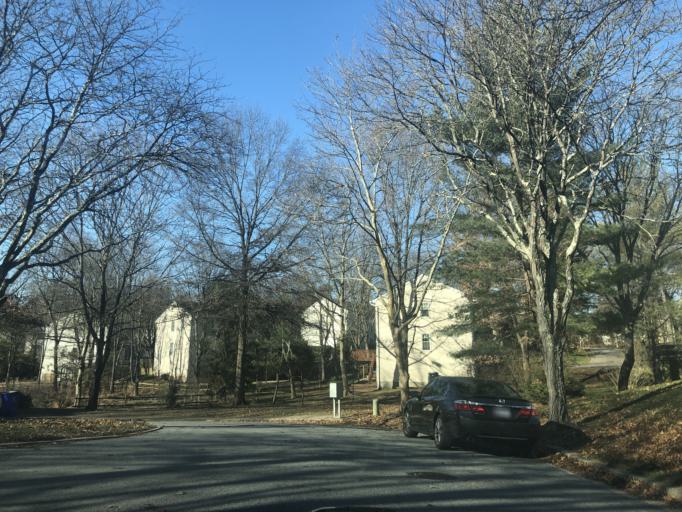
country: US
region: Maryland
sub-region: Howard County
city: Columbia
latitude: 39.2031
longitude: -76.8302
